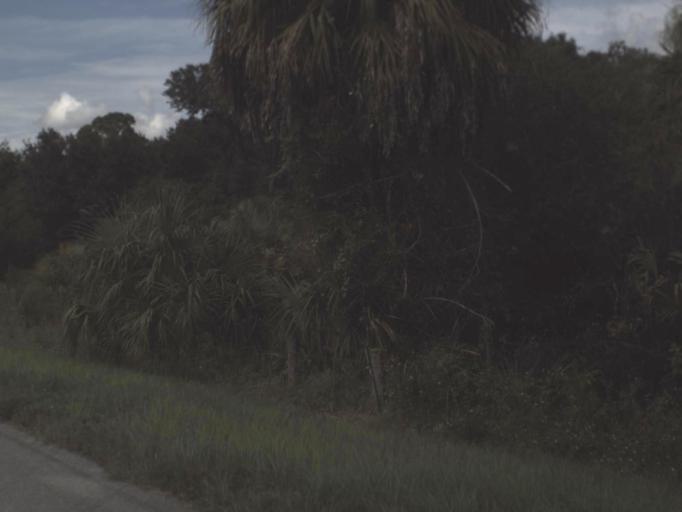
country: US
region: Florida
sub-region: Highlands County
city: Placid Lakes
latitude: 27.2092
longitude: -81.4632
